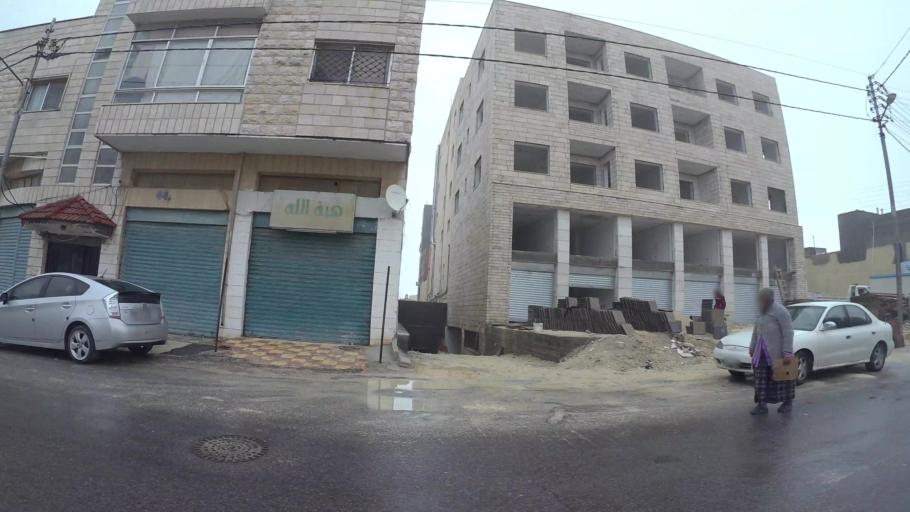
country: JO
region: Amman
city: Al Jubayhah
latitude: 32.0192
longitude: 35.8378
